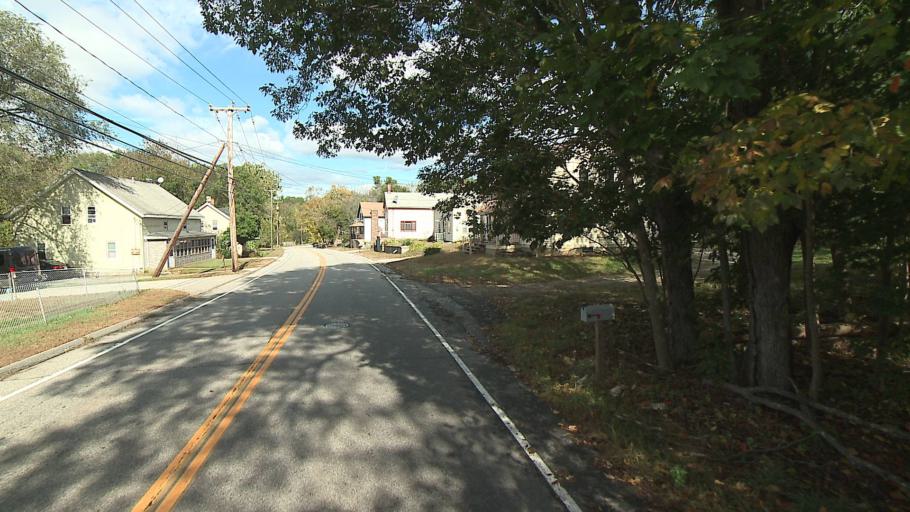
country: US
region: Connecticut
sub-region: Windham County
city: Killingly Center
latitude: 41.8618
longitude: -71.8824
